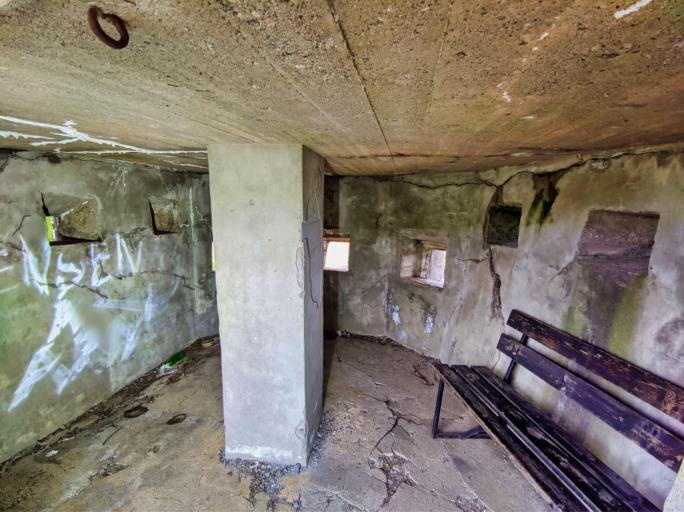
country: NO
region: Ostfold
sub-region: Eidsberg
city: Mysen
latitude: 59.5618
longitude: 11.3434
